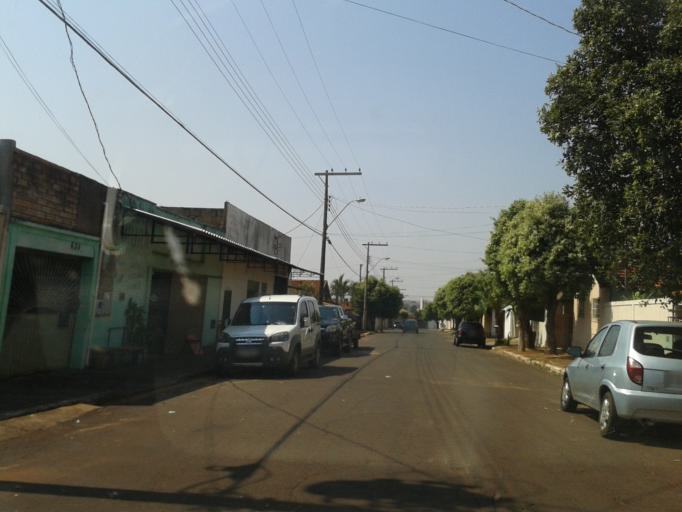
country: BR
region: Minas Gerais
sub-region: Ituiutaba
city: Ituiutaba
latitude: -18.9724
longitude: -49.4751
